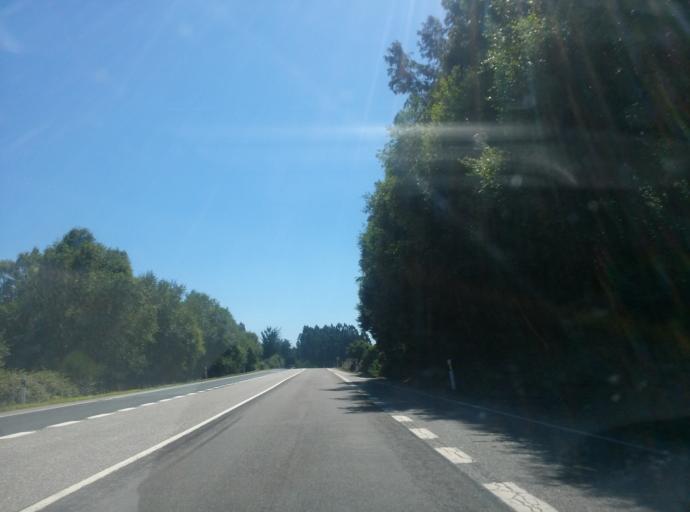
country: ES
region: Galicia
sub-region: Provincia de Lugo
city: Castro de Rei
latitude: 43.1587
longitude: -7.3839
